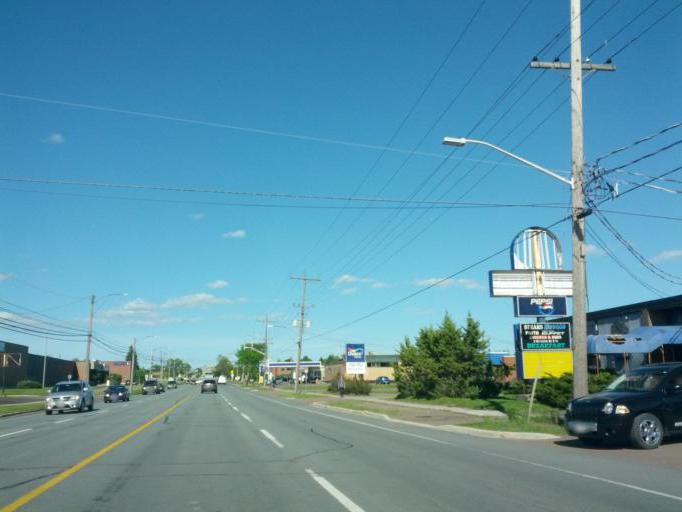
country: CA
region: New Brunswick
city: Moncton
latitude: 46.0853
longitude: -64.8100
